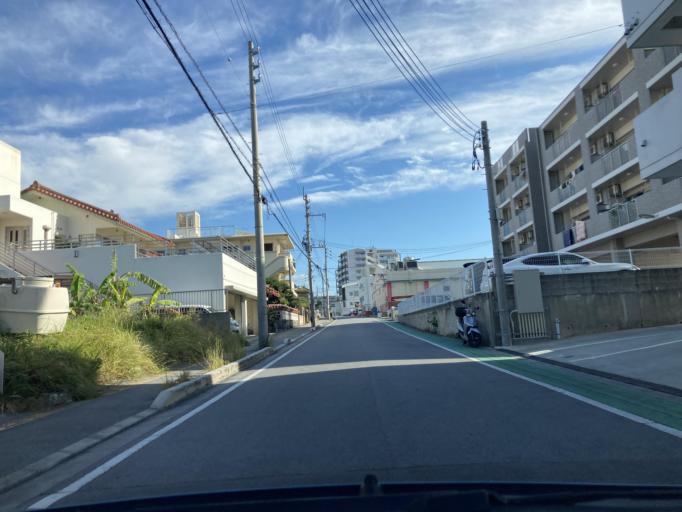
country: JP
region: Okinawa
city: Tomigusuku
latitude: 26.1937
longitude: 127.7138
